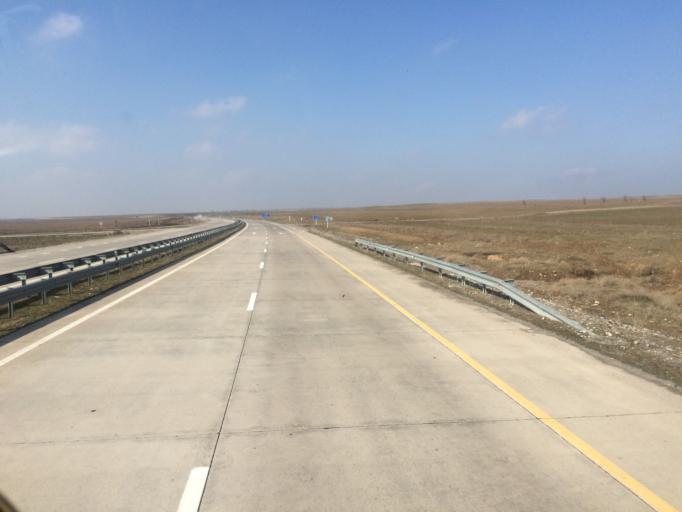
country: KZ
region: Ongtustik Qazaqstan
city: Shymkent
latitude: 42.4874
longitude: 69.5202
